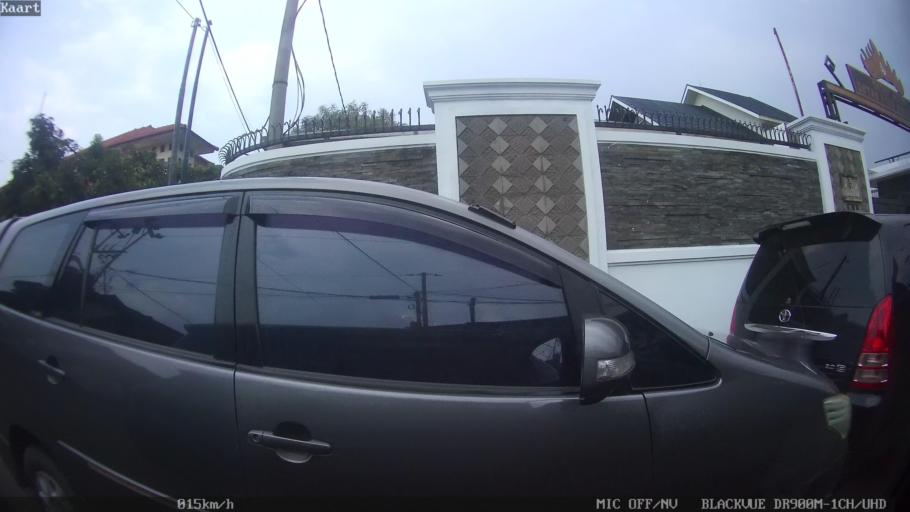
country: ID
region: Lampung
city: Bandarlampung
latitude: -5.4247
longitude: 105.2643
